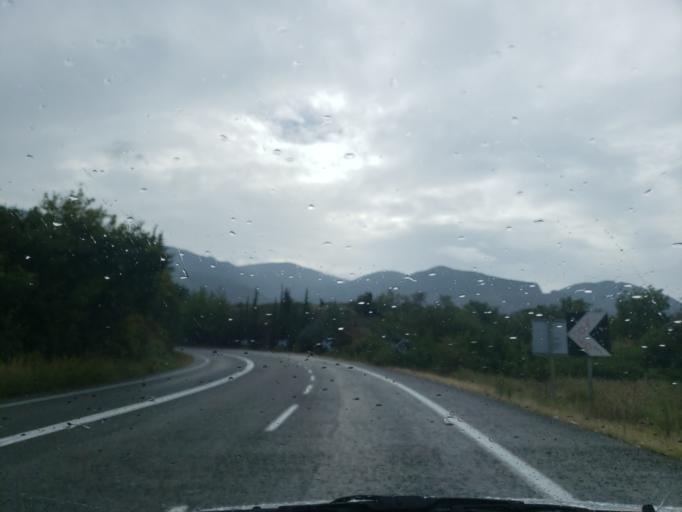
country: GR
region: Central Greece
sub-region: Nomos Fthiotidos
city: Anthili
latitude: 38.7935
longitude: 22.4740
